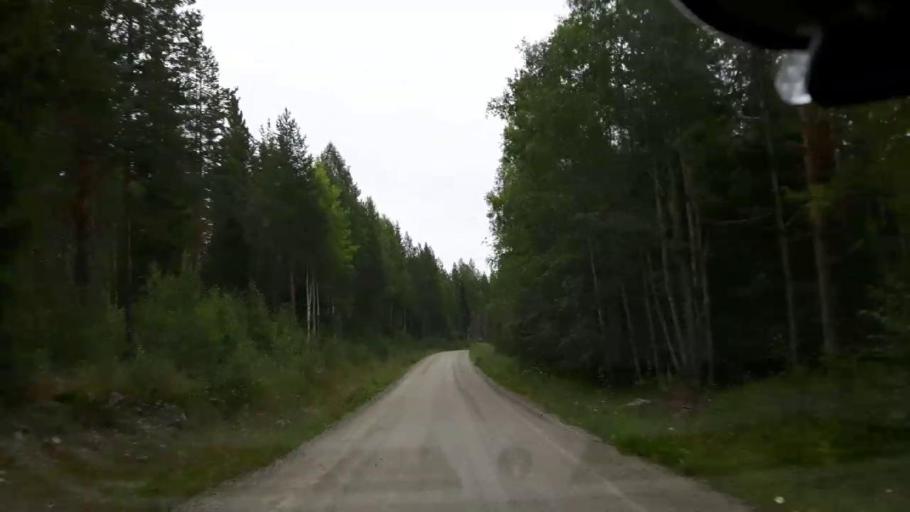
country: SE
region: Jaemtland
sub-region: Braecke Kommun
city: Braecke
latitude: 62.8264
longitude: 15.7057
